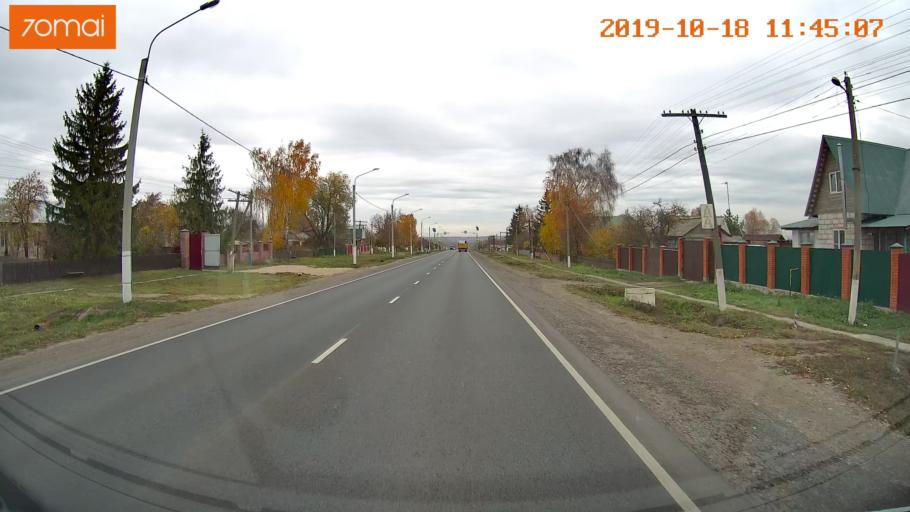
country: RU
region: Rjazan
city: Mikhaylov
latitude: 54.2078
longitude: 38.9662
